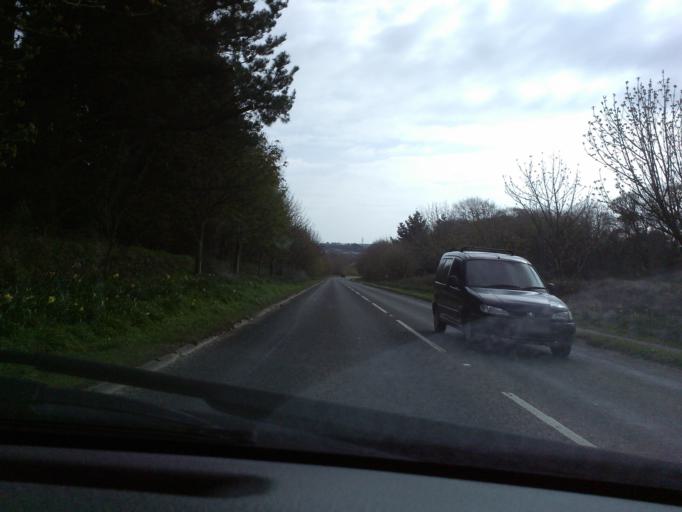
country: GB
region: England
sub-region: Cornwall
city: Penzance
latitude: 50.1238
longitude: -5.5498
